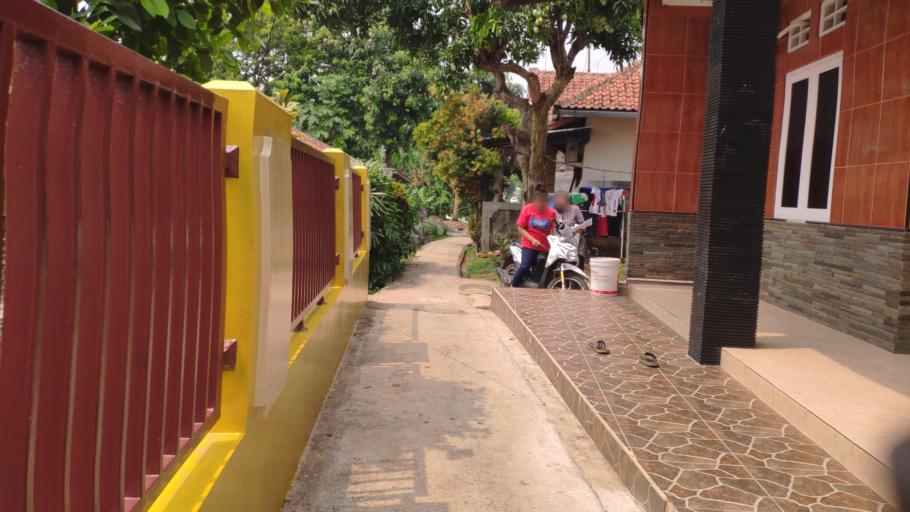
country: ID
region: West Java
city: Depok
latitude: -6.3707
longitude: 106.8052
